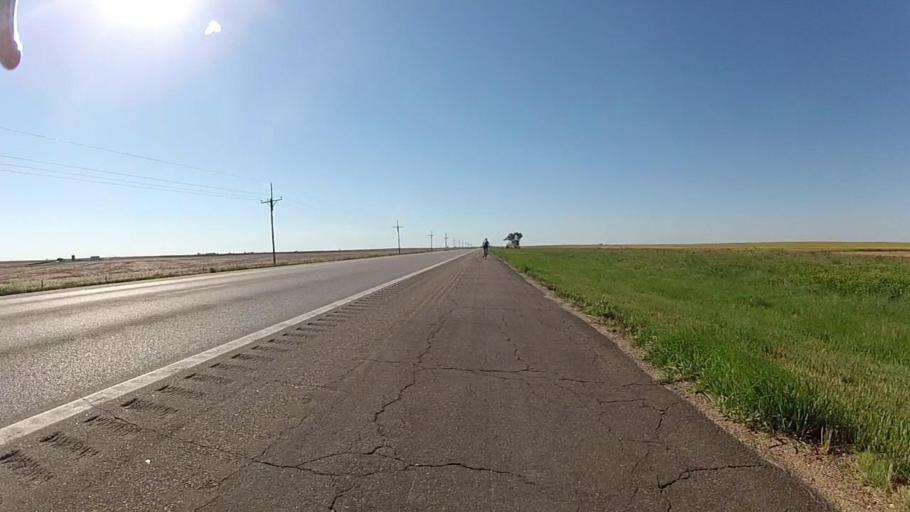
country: US
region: Kansas
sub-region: Ford County
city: Dodge City
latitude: 37.5954
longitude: -99.6944
